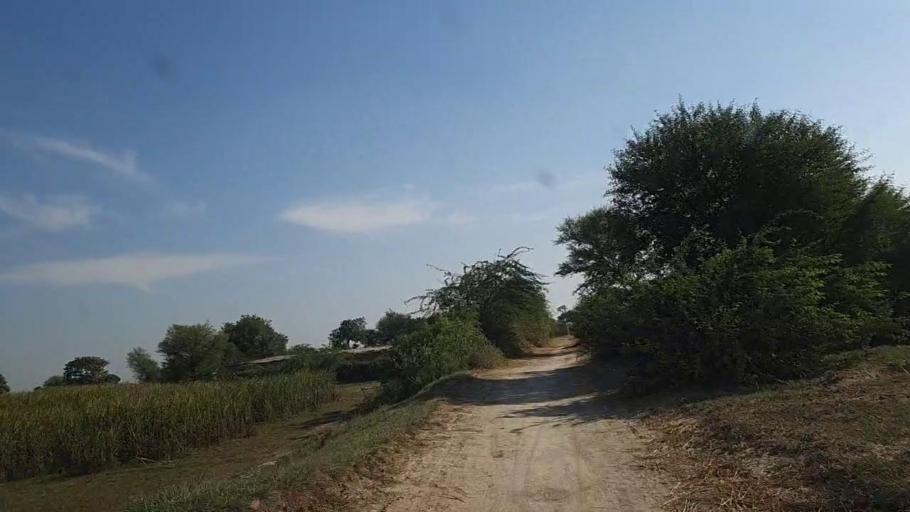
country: PK
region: Sindh
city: Bulri
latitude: 24.8585
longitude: 68.2881
